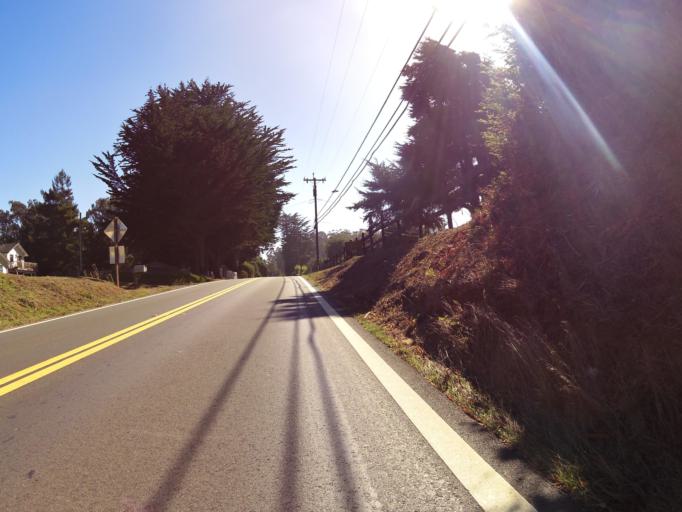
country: US
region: California
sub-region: Mendocino County
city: Fort Bragg
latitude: 39.5261
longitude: -123.7603
